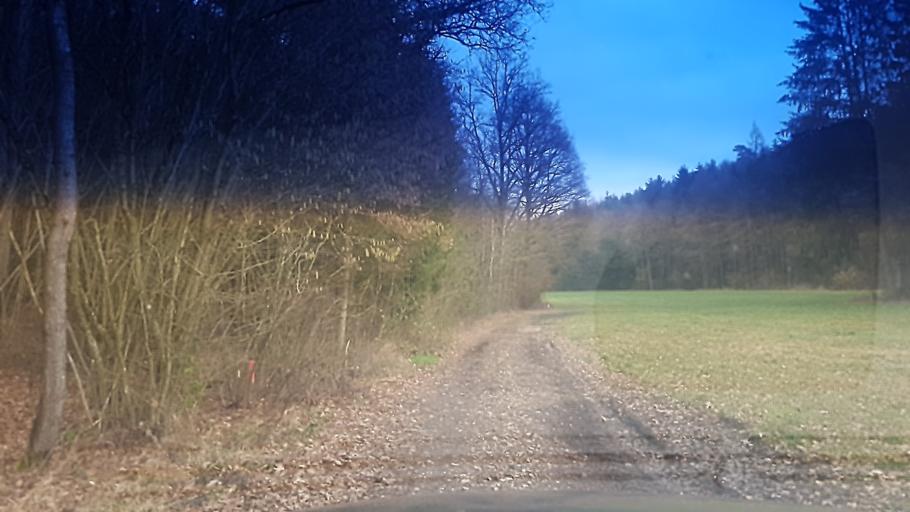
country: DE
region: Bavaria
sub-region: Upper Franconia
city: Zapfendorf
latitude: 49.9753
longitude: 10.9464
